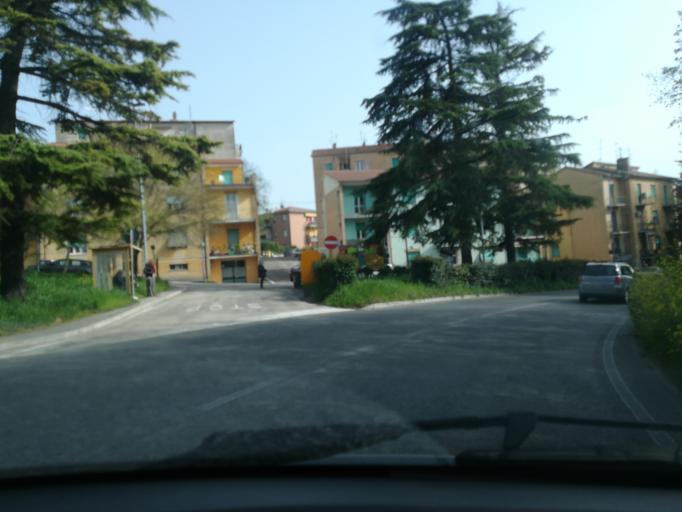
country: IT
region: The Marches
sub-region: Provincia di Macerata
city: Macerata
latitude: 43.2927
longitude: 13.4695
